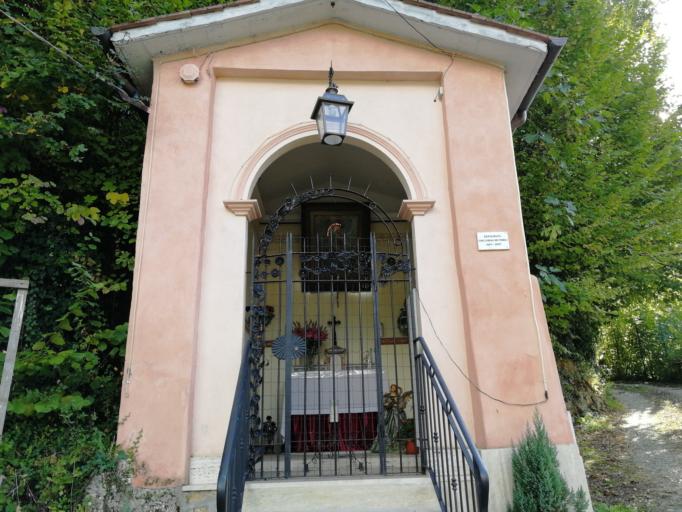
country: IT
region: Latium
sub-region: Citta metropolitana di Roma Capitale
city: Subiaco
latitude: 41.9219
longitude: 13.0981
